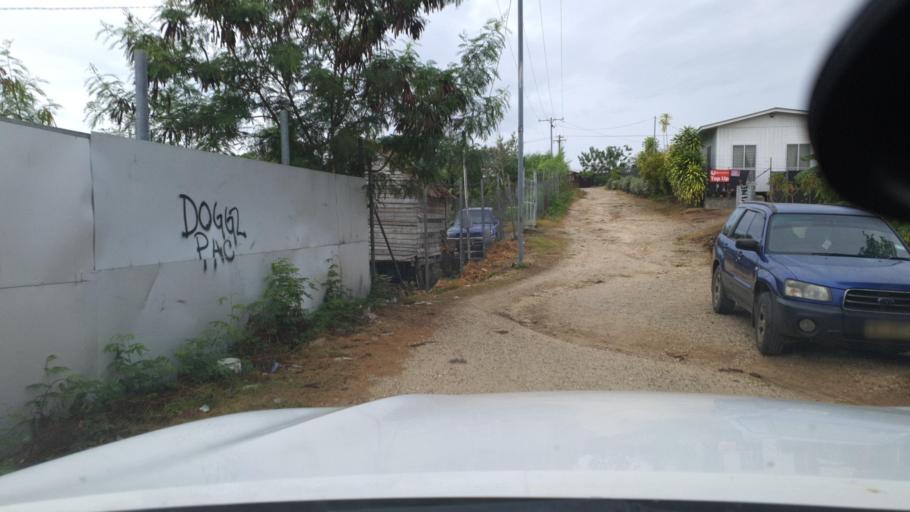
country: SB
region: Guadalcanal
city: Honiara
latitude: -9.4424
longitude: 159.9652
